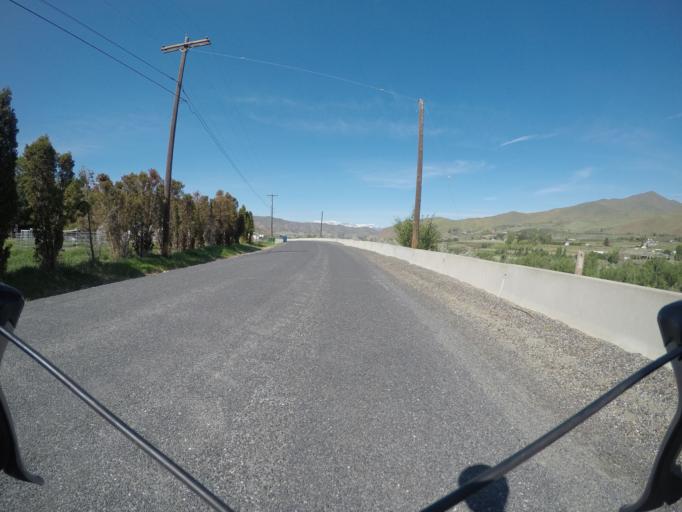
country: US
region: Washington
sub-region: Chelan County
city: West Wenatchee
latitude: 47.4773
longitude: -120.3839
